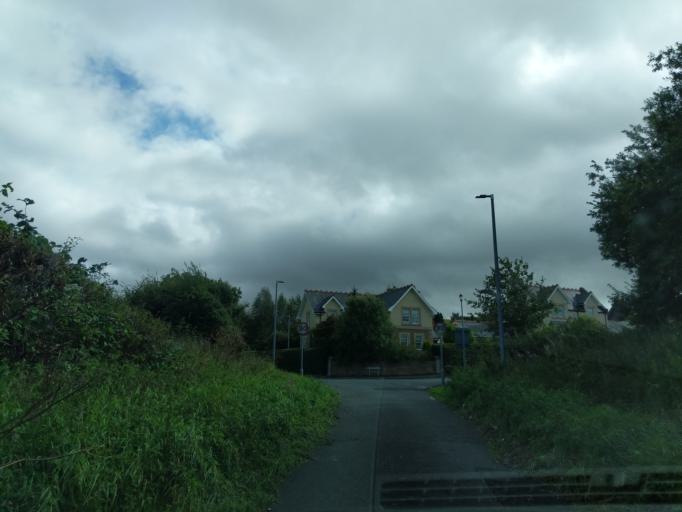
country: GB
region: Scotland
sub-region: The Scottish Borders
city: Kelso
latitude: 55.5648
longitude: -2.4681
